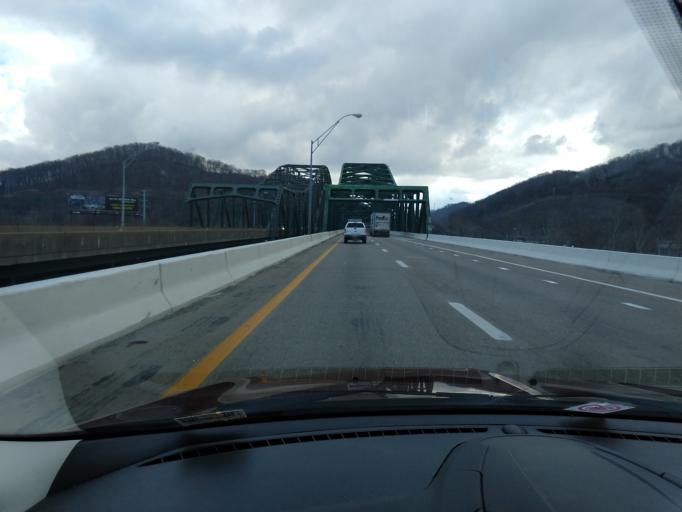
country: US
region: West Virginia
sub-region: Kanawha County
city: Rand
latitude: 38.3083
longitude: -81.5626
